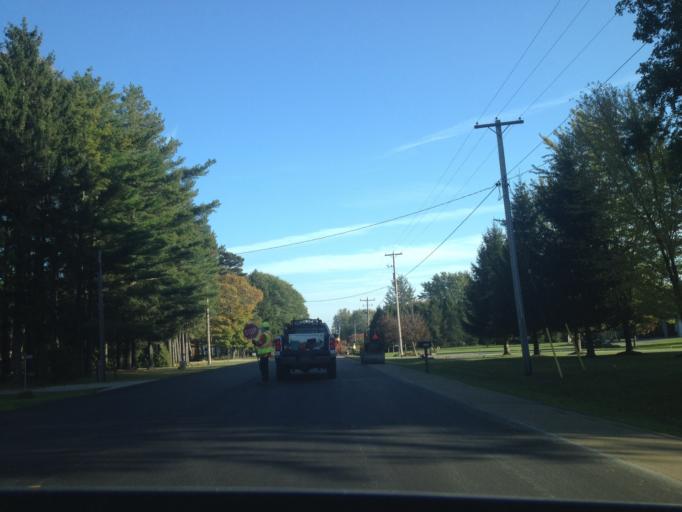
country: CA
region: Ontario
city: Delaware
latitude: 42.5757
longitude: -81.5722
